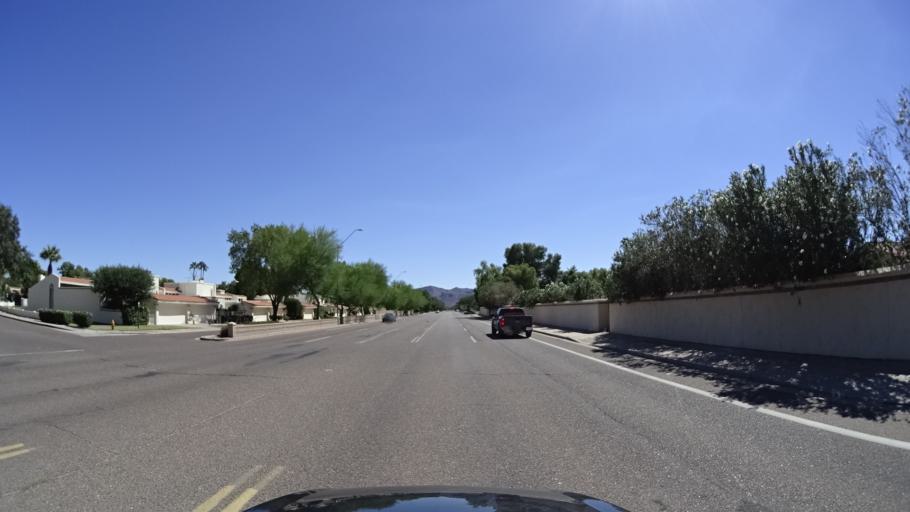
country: US
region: Arizona
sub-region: Maricopa County
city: Paradise Valley
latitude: 33.5914
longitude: -111.9606
